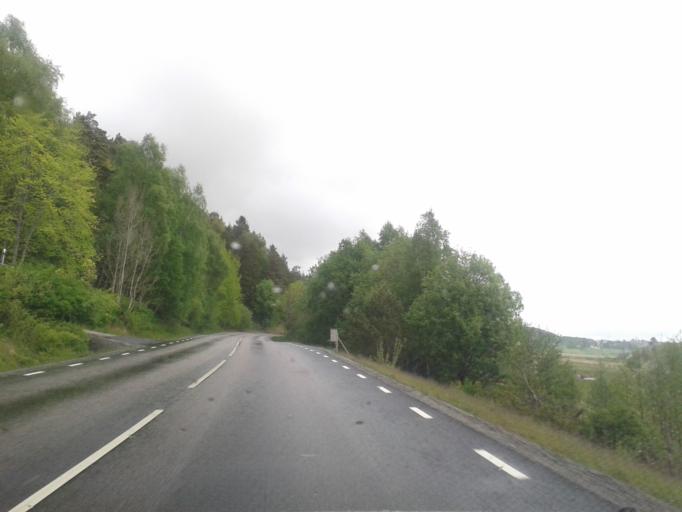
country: SE
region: Vaestra Goetaland
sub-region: Ale Kommun
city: Alvangen
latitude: 57.9617
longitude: 12.0978
